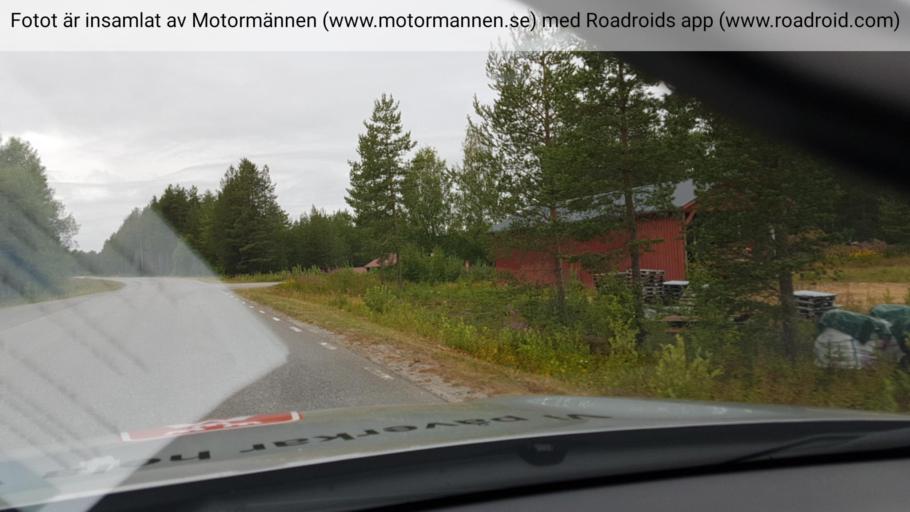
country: SE
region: Norrbotten
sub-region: Bodens Kommun
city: Boden
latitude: 65.8153
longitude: 21.6079
